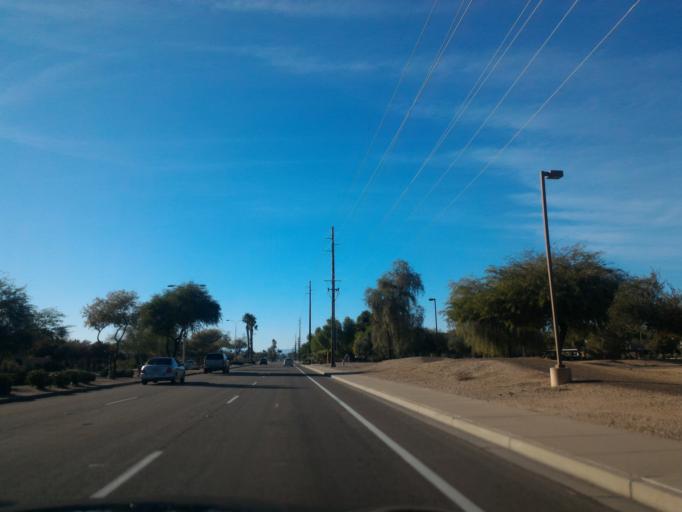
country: US
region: Arizona
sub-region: Maricopa County
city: Guadalupe
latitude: 33.3055
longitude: -111.9358
